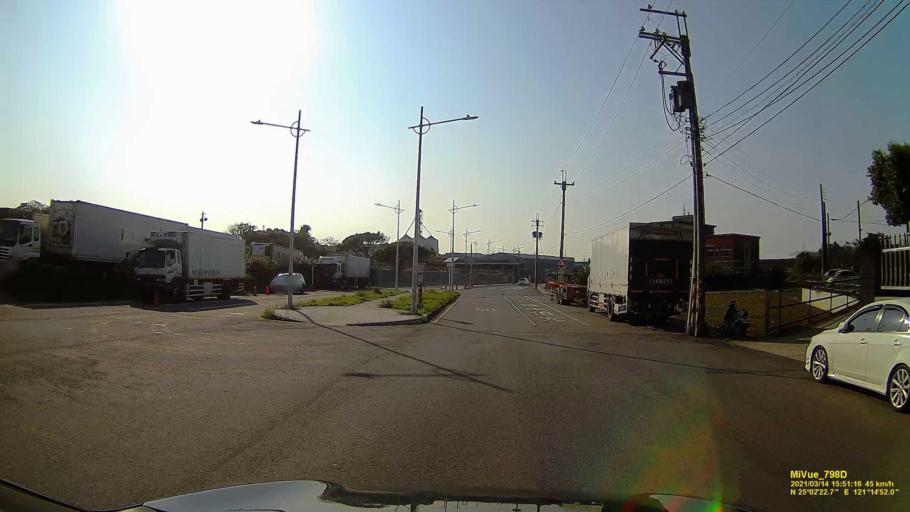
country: TW
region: Taiwan
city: Taoyuan City
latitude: 25.0399
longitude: 121.2473
